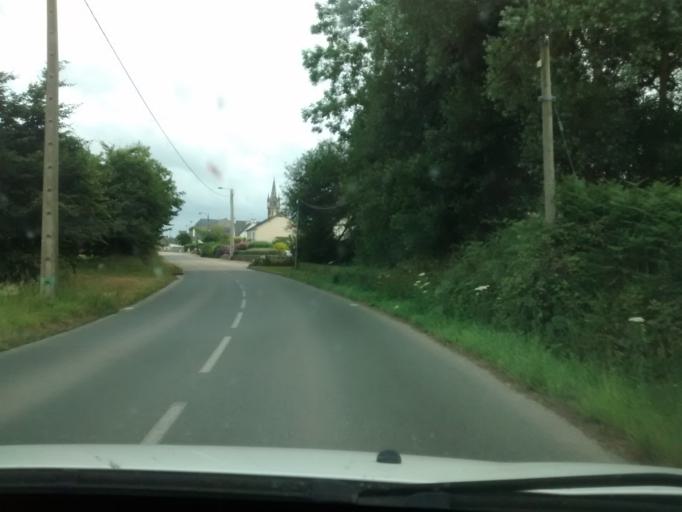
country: FR
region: Brittany
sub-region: Departement des Cotes-d'Armor
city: Plouguiel
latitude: 48.8007
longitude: -3.2395
